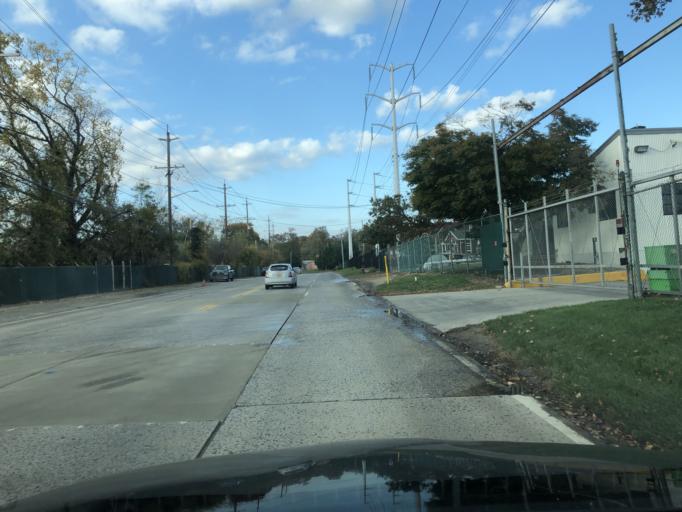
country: US
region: New York
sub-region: Nassau County
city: Glenwood Landing
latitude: 40.8296
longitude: -73.6480
